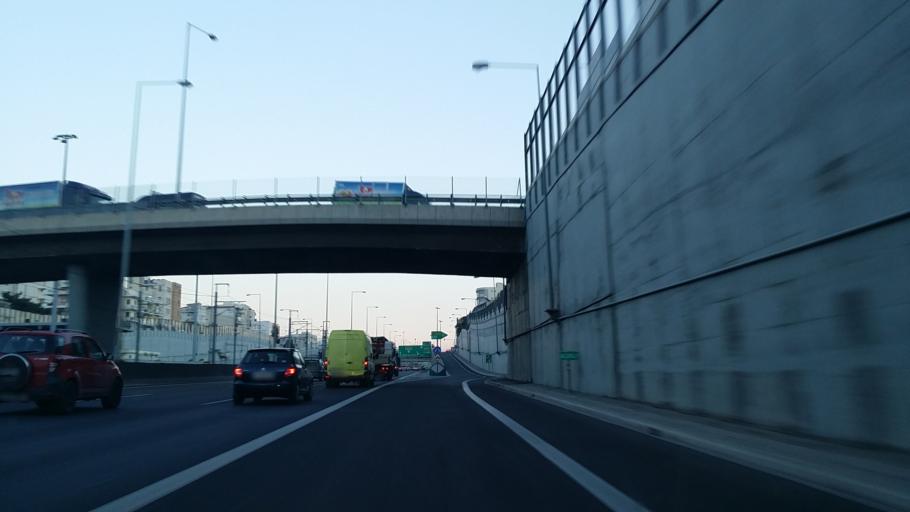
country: GR
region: Attica
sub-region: Nomarchia Athinas
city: Irakleio
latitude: 38.0587
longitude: 23.7672
